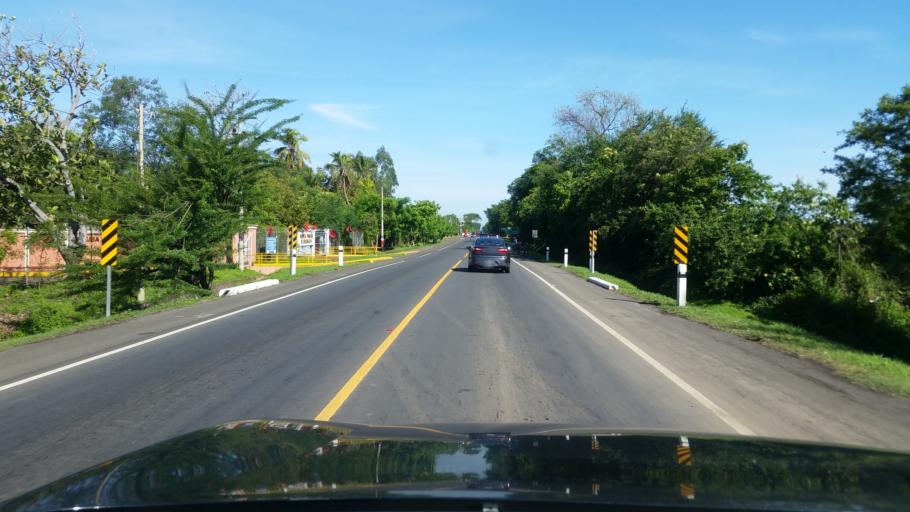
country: NI
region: Chinandega
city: Chichigalpa
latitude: 12.5903
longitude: -87.0210
